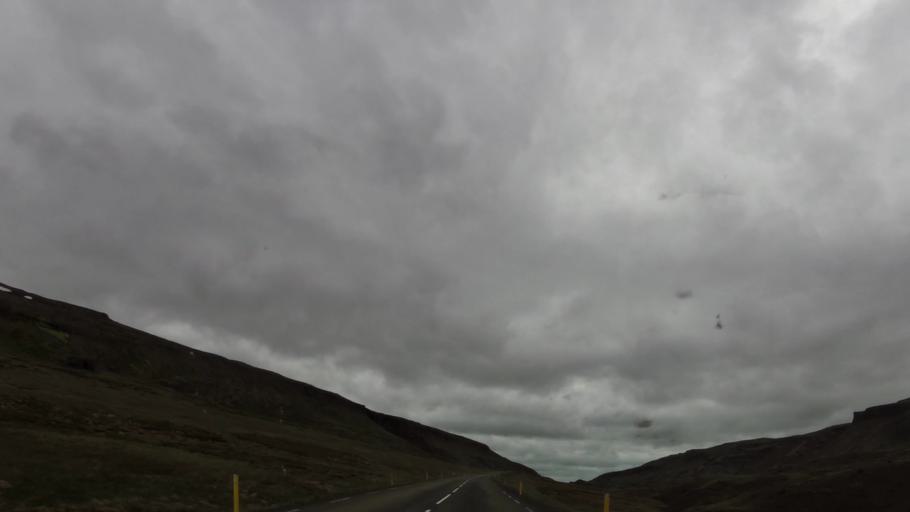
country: IS
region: West
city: Borgarnes
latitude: 65.3311
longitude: -21.7460
